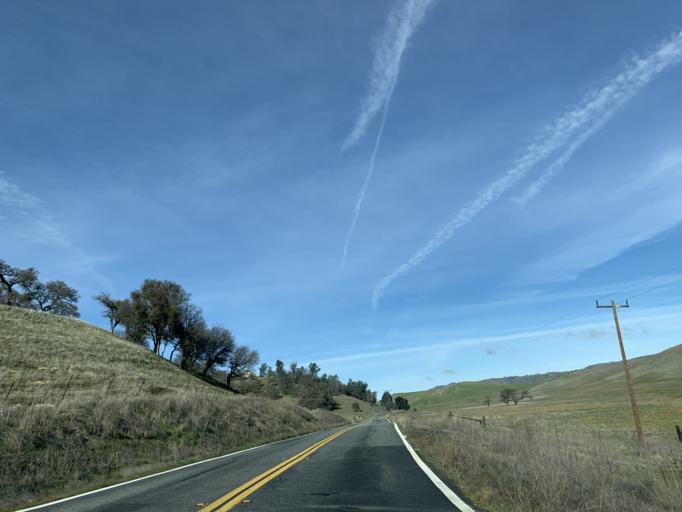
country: US
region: California
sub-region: Monterey County
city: Soledad
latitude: 36.5549
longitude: -121.1695
